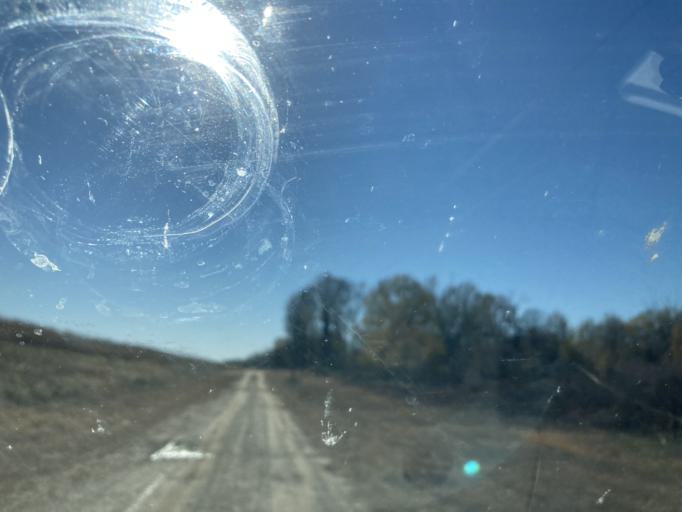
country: US
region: Mississippi
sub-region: Sharkey County
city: Rolling Fork
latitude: 32.7515
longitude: -90.6606
